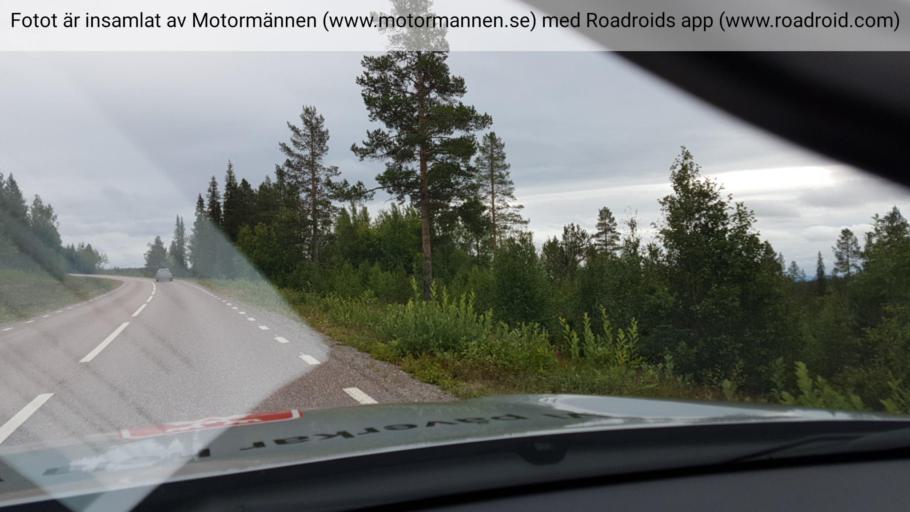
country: SE
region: Norrbotten
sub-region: Gallivare Kommun
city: Gaellivare
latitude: 67.0471
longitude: 21.6159
